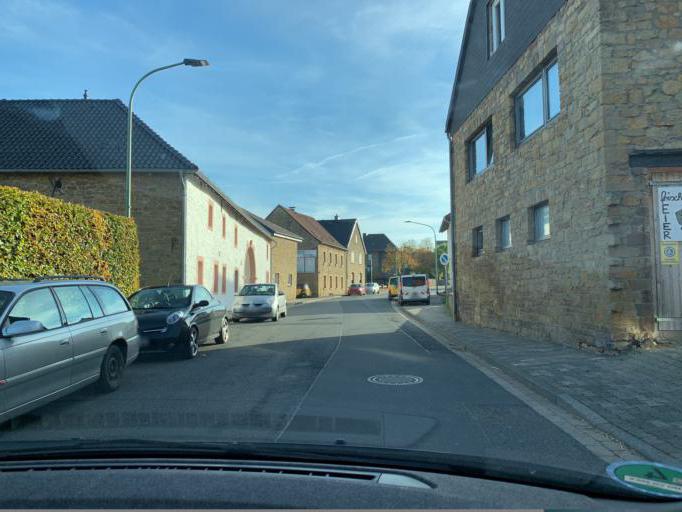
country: DE
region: North Rhine-Westphalia
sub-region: Regierungsbezirk Koln
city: Nideggen
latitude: 50.6800
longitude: 6.5192
